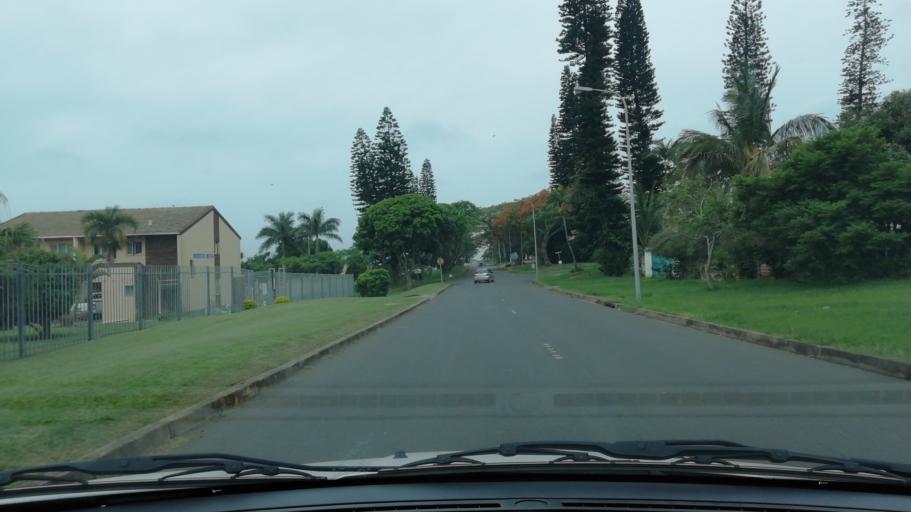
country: ZA
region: KwaZulu-Natal
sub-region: uThungulu District Municipality
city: Empangeni
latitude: -28.7399
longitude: 31.8881
